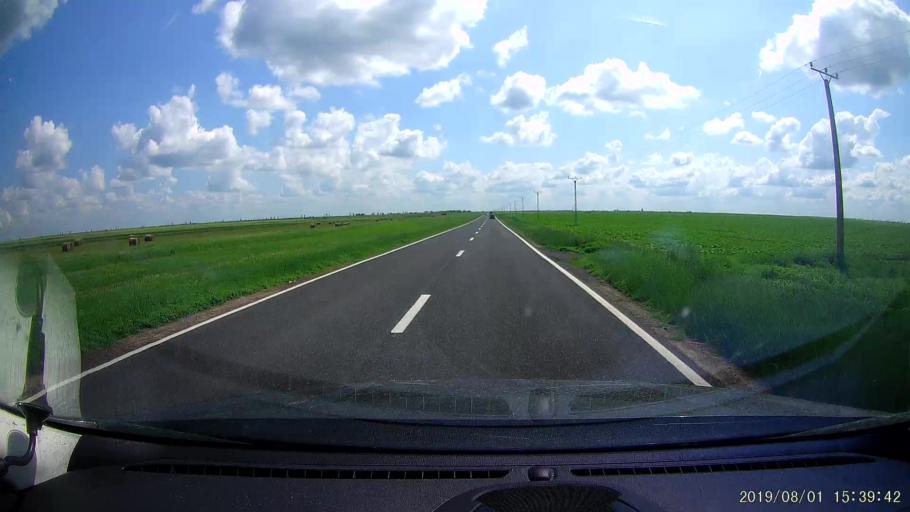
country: RO
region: Braila
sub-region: Comuna Baraganul
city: Baraganul
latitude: 44.8516
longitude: 27.5546
